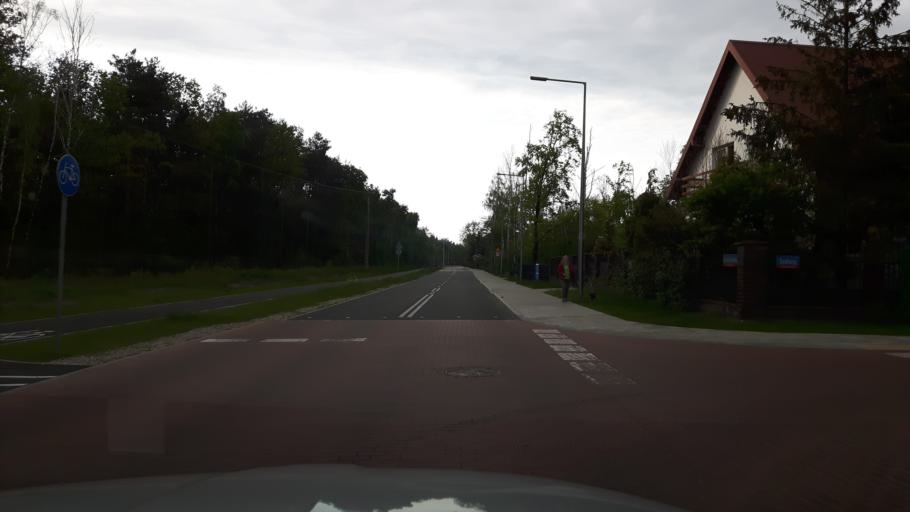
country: PL
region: Masovian Voivodeship
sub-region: Warszawa
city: Rembertow
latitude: 52.2651
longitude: 21.1485
